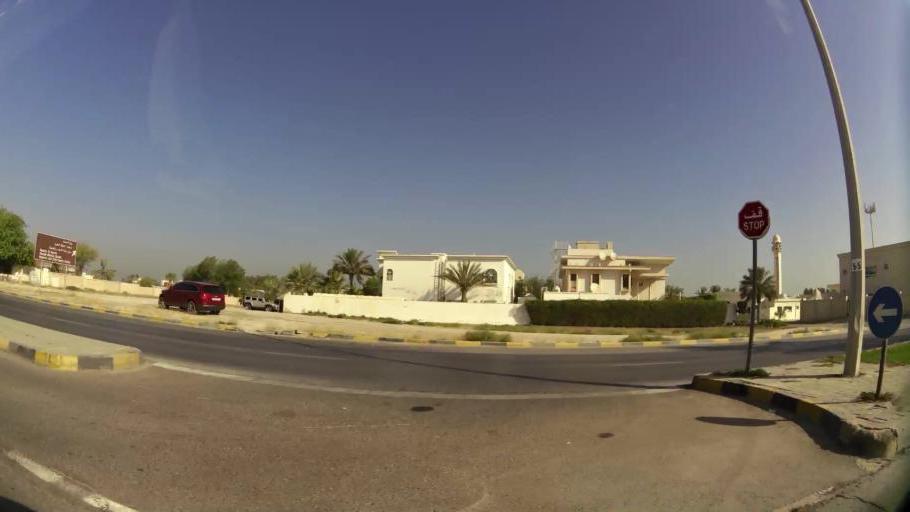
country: AE
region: Ajman
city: Ajman
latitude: 25.3811
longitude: 55.4059
